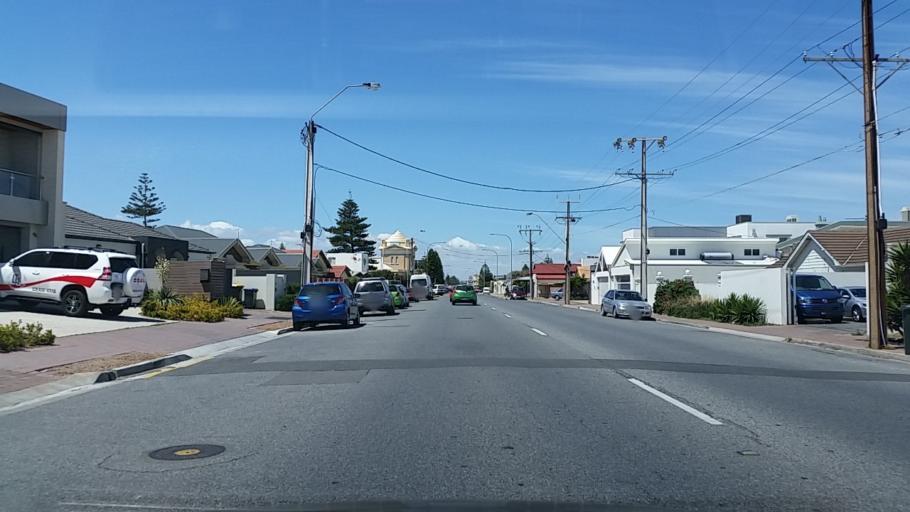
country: AU
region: South Australia
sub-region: Charles Sturt
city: Henley Beach
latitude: -34.9155
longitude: 138.4932
